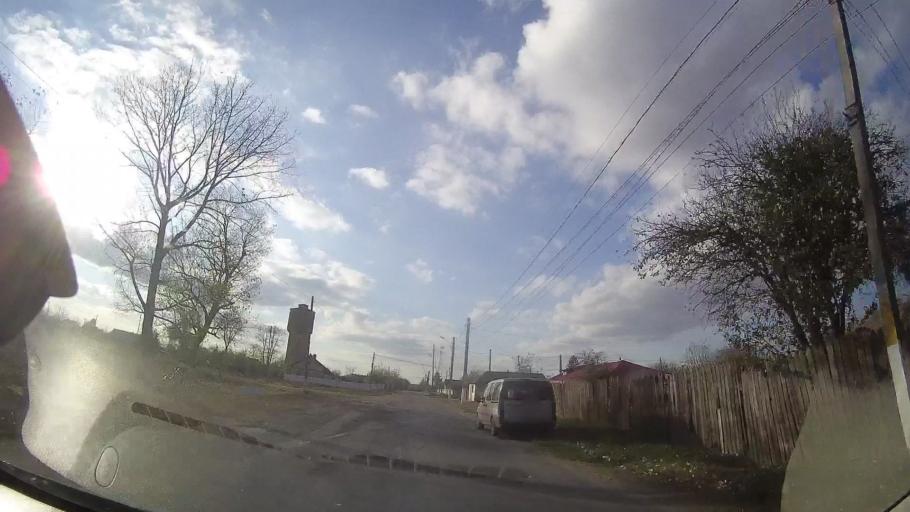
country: RO
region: Constanta
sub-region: Comuna Negru Voda
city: Negru Voda
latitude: 43.8194
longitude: 28.2249
